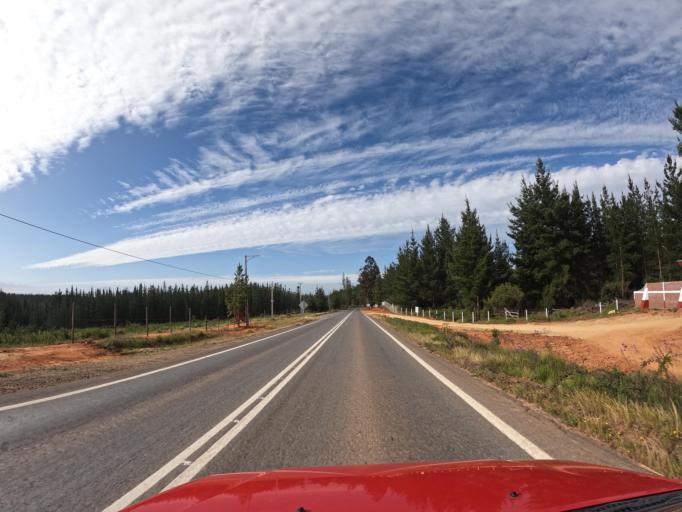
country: CL
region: O'Higgins
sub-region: Provincia de Colchagua
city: Santa Cruz
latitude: -34.2986
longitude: -71.8230
